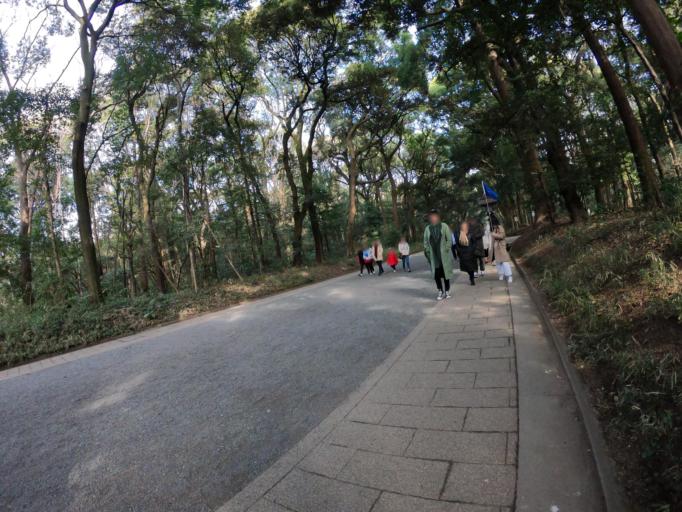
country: JP
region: Chiba
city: Ichihara
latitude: 35.4606
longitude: 140.0173
